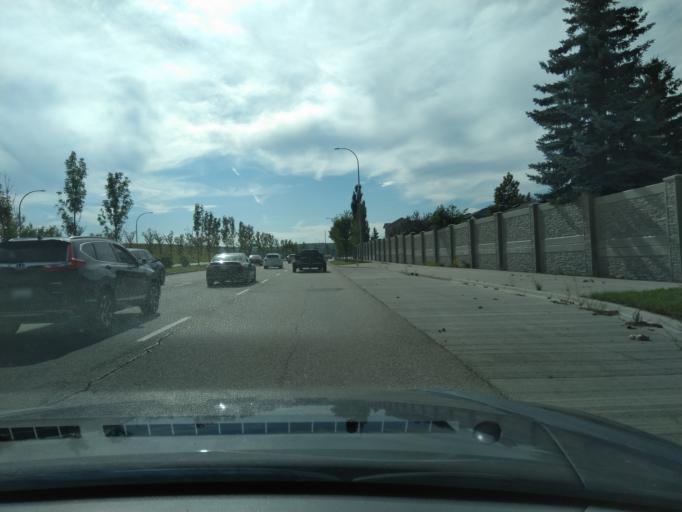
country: CA
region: Alberta
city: Calgary
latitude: 51.1419
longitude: -114.0518
